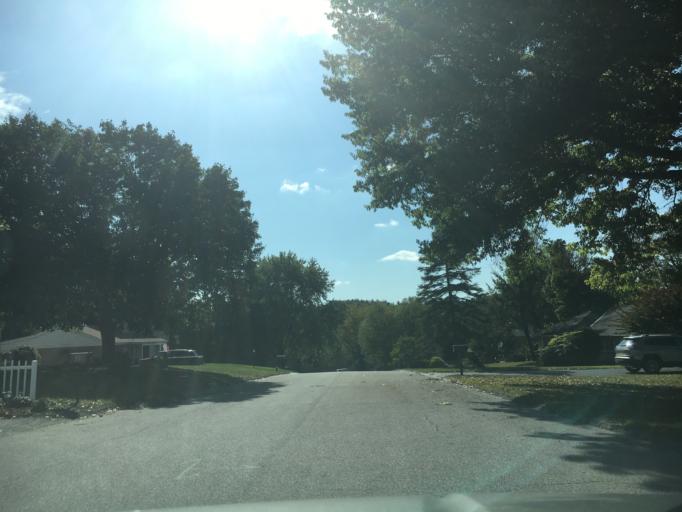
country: US
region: Pennsylvania
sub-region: York County
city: Grantley
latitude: 39.9427
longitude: -76.7146
